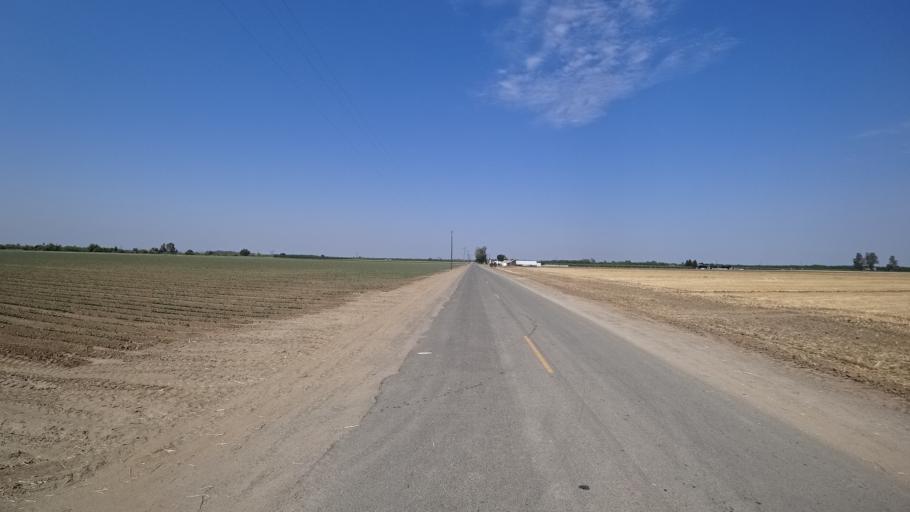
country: US
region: California
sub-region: Fresno County
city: Riverdale
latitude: 36.3948
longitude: -119.7938
